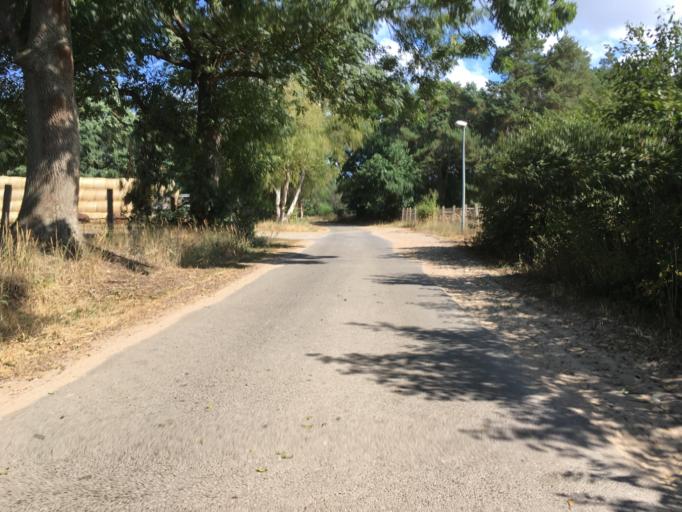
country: DE
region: Brandenburg
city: Zehdenick
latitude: 52.9896
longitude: 13.3789
